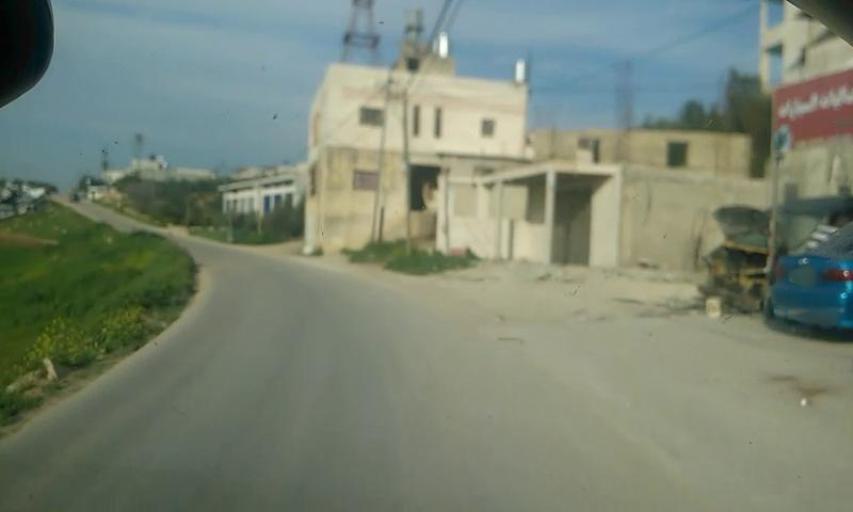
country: PS
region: West Bank
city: Bayt Ula
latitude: 31.6055
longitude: 35.0150
